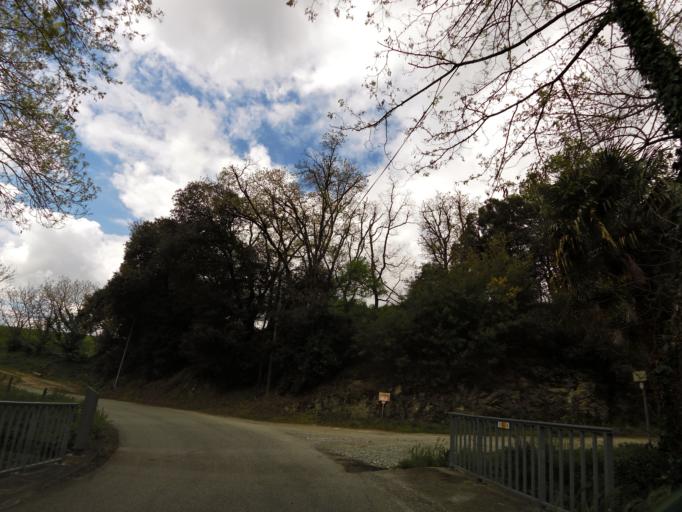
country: FR
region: Languedoc-Roussillon
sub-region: Departement de l'Aude
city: Villepinte
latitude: 43.3516
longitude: 2.0872
